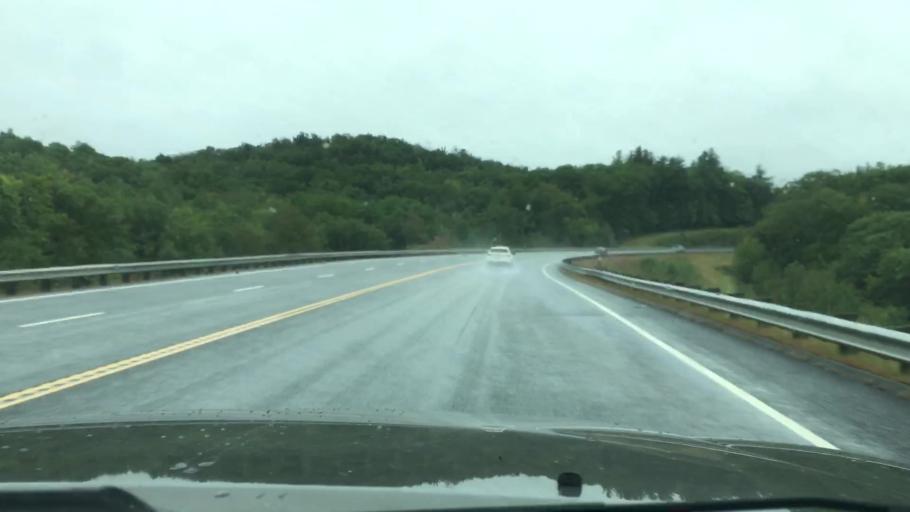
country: US
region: New Hampshire
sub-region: Cheshire County
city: Harrisville
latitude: 43.0103
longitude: -72.1423
